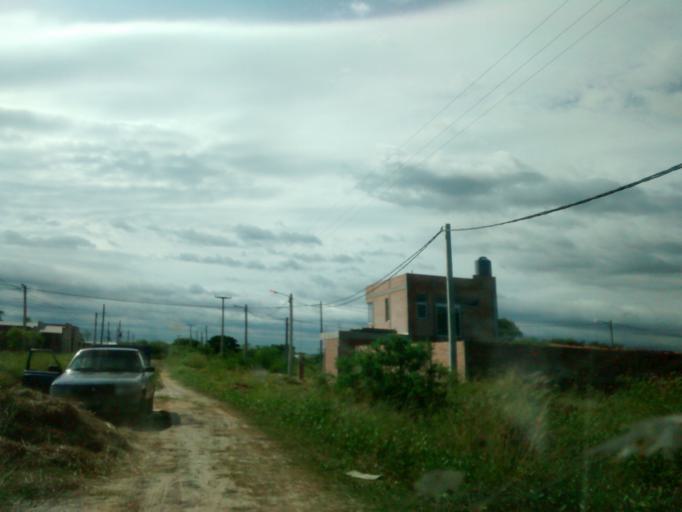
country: AR
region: Chaco
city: Resistencia
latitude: -27.4081
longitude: -58.9702
